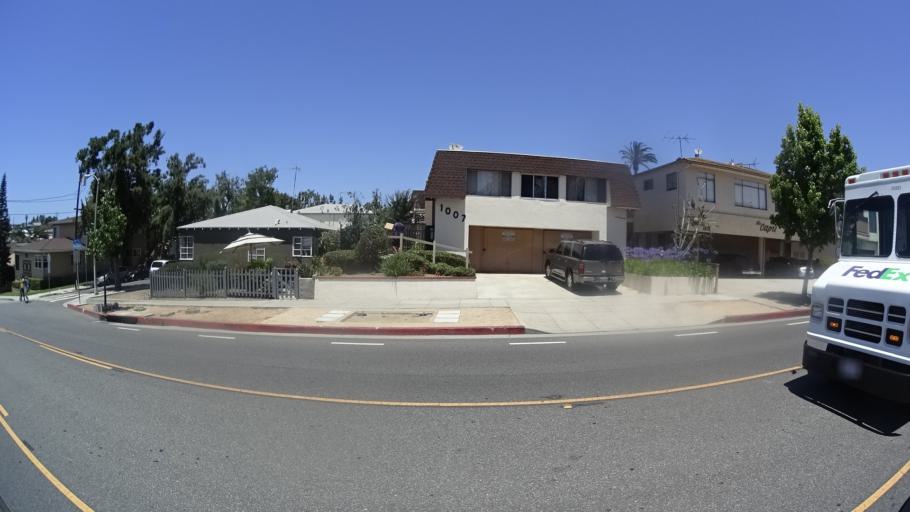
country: US
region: California
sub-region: Los Angeles County
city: Santa Monica
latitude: 34.0076
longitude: -118.4751
